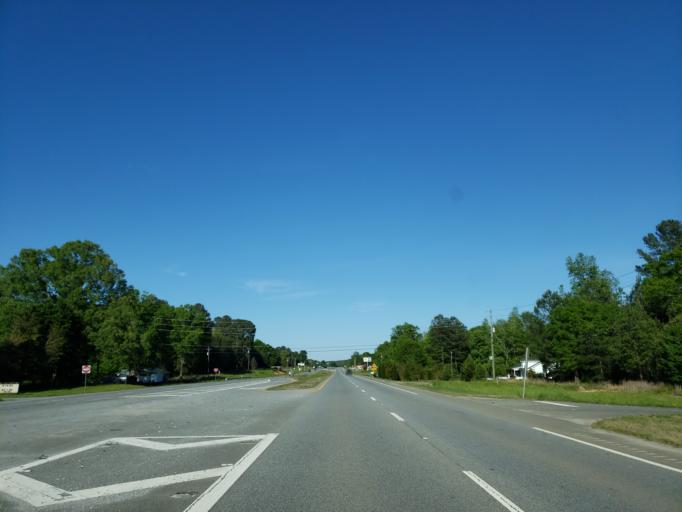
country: US
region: Georgia
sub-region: Polk County
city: Aragon
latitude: 34.0055
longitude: -85.1463
